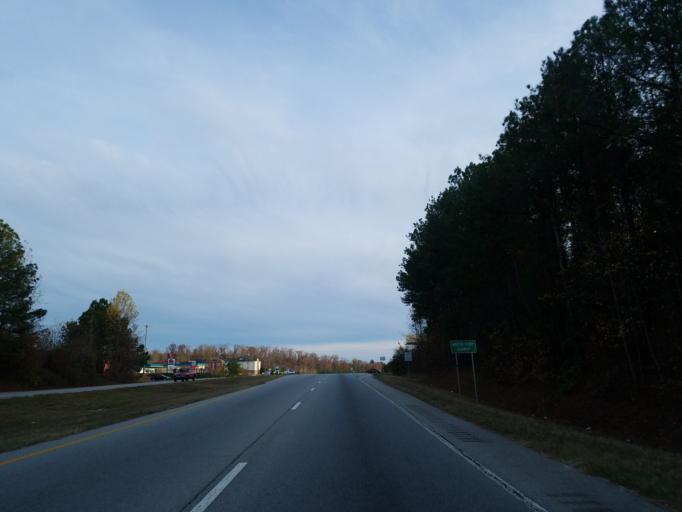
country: US
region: Georgia
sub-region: Haralson County
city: Bremen
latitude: 33.6949
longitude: -85.1550
